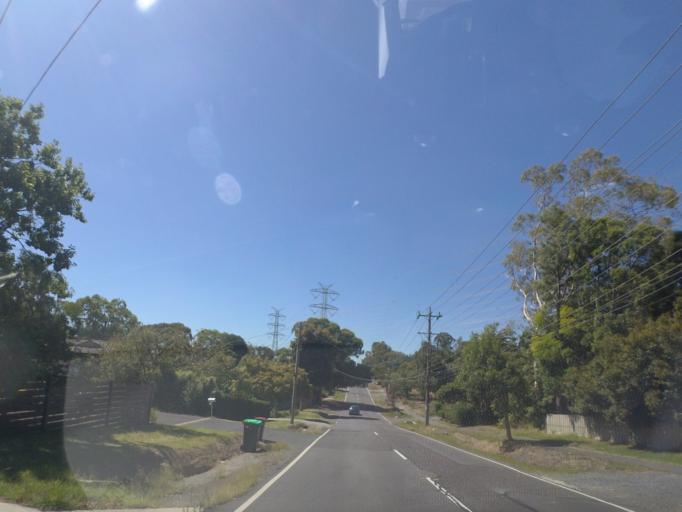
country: AU
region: Victoria
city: Mitcham
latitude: -37.8049
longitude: 145.2148
